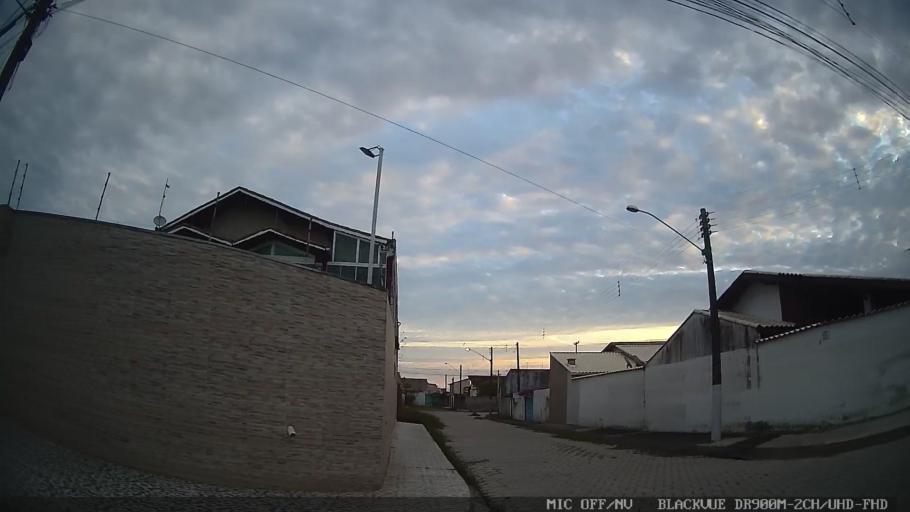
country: BR
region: Sao Paulo
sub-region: Itanhaem
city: Itanhaem
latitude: -24.1721
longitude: -46.7773
